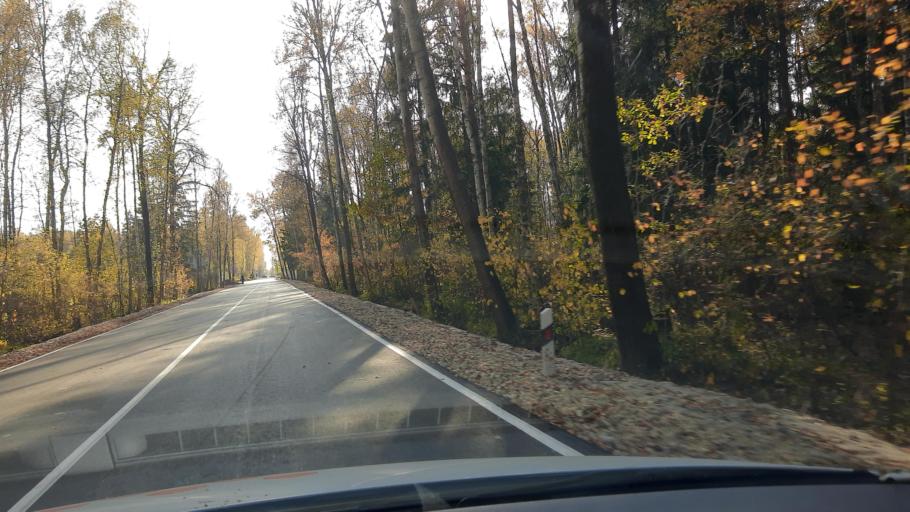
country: RU
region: Moskovskaya
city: Imeni Vorovskogo
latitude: 55.7903
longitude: 38.3659
